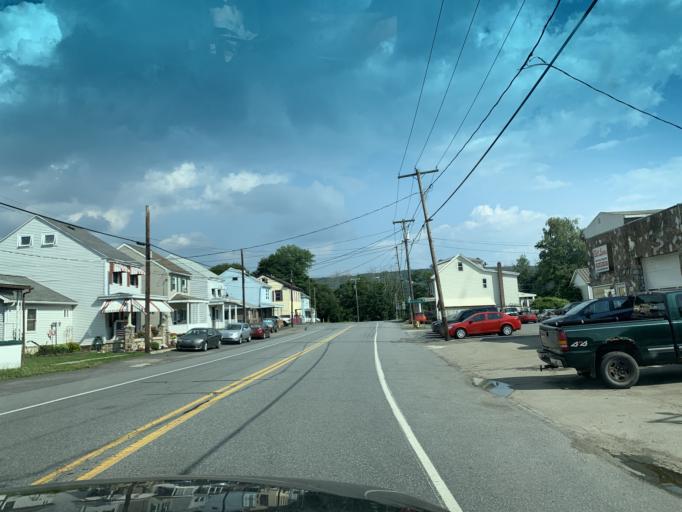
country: US
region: Pennsylvania
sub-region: Schuylkill County
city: Ashland
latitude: 40.7709
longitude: -76.3264
